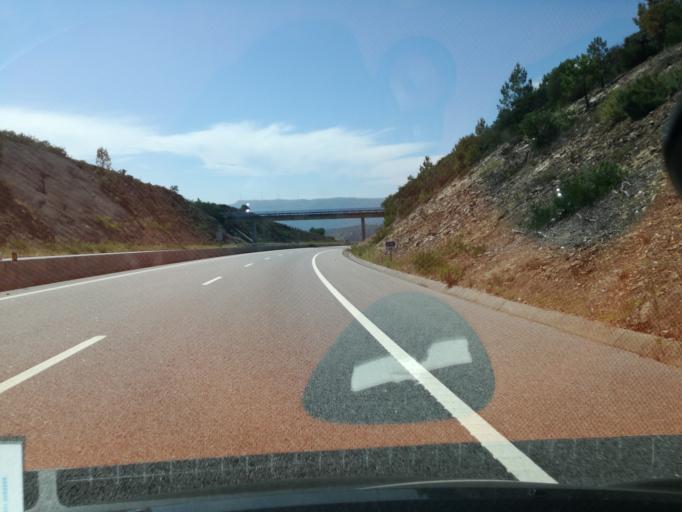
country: PT
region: Viana do Castelo
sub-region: Caminha
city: Vila Praia de Ancora
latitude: 41.8303
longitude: -8.7869
